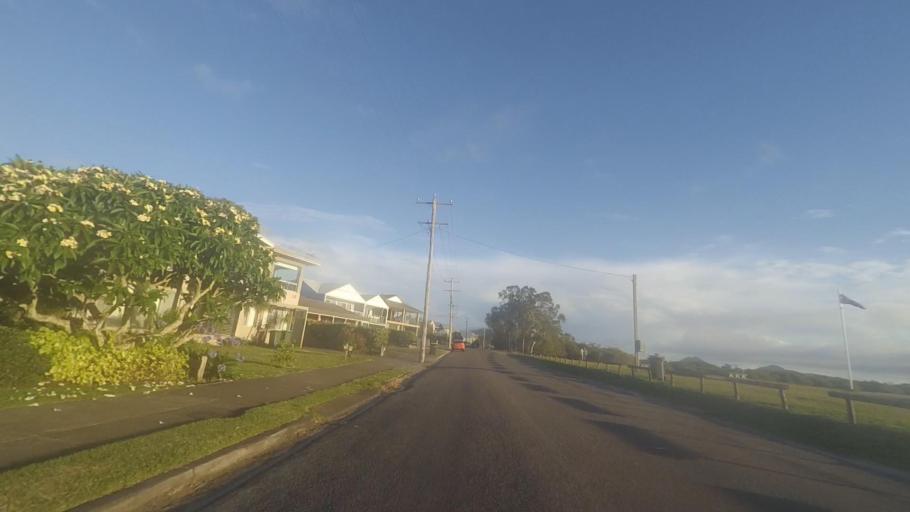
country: AU
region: New South Wales
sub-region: Great Lakes
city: Hawks Nest
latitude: -32.6709
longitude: 152.1717
